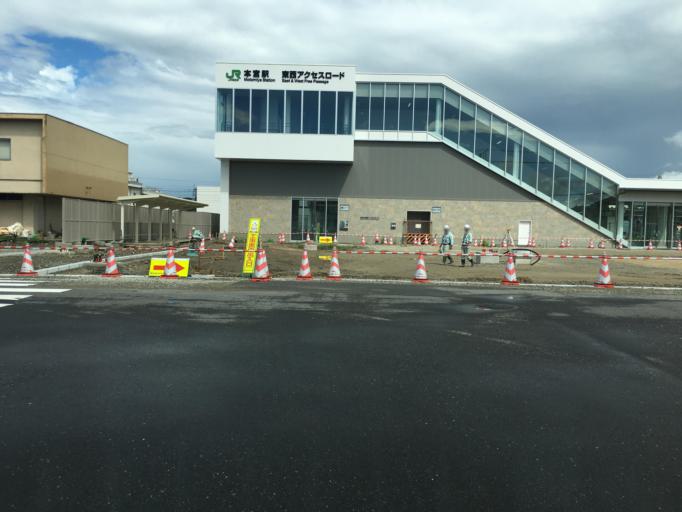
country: JP
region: Fukushima
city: Motomiya
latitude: 37.5141
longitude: 140.3986
